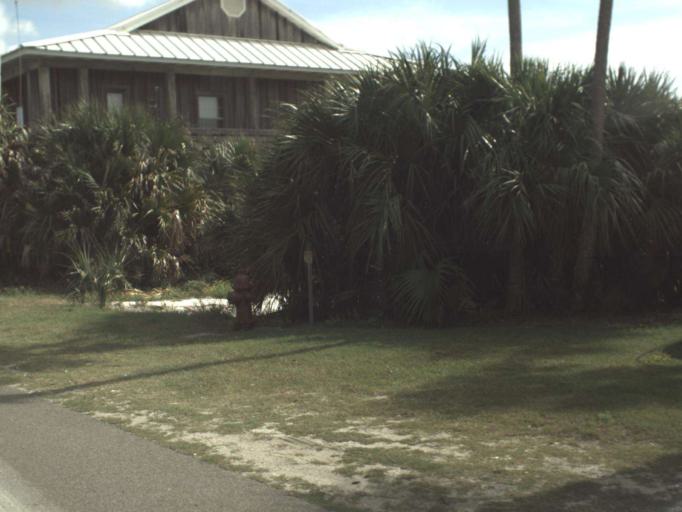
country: US
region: Florida
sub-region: Bay County
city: Mexico Beach
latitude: 29.9219
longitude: -85.3850
